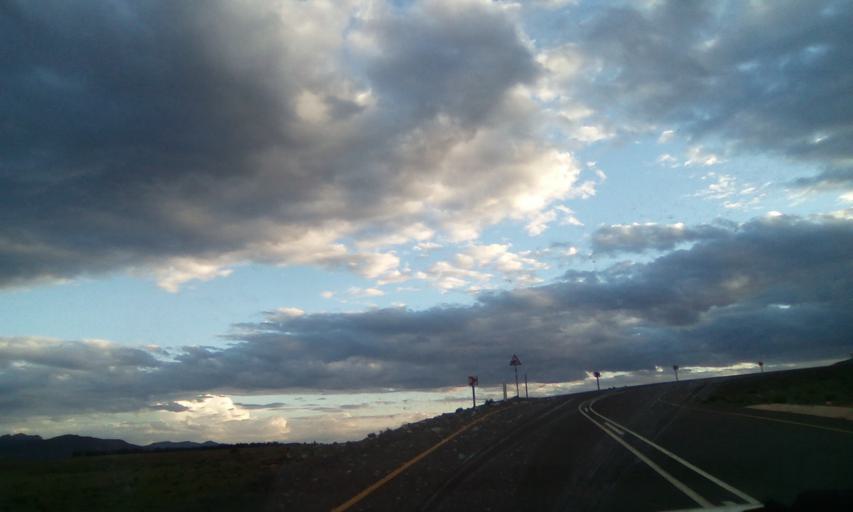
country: LS
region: Maseru
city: Nako
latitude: -29.8168
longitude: 28.0363
